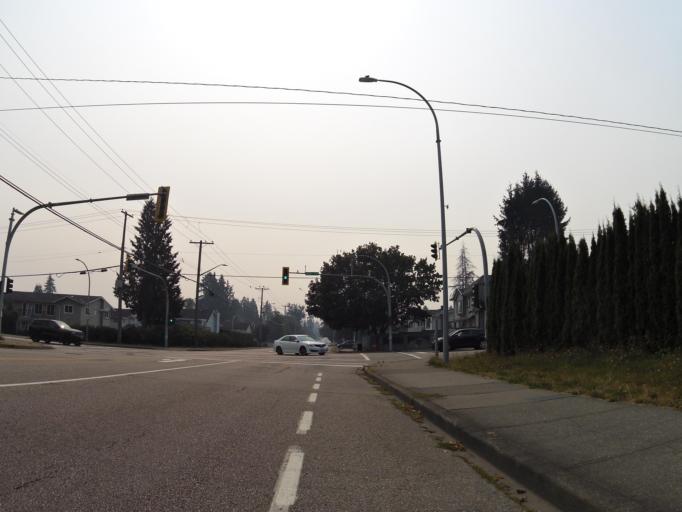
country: CA
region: British Columbia
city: Surrey
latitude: 49.1270
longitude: -122.8567
